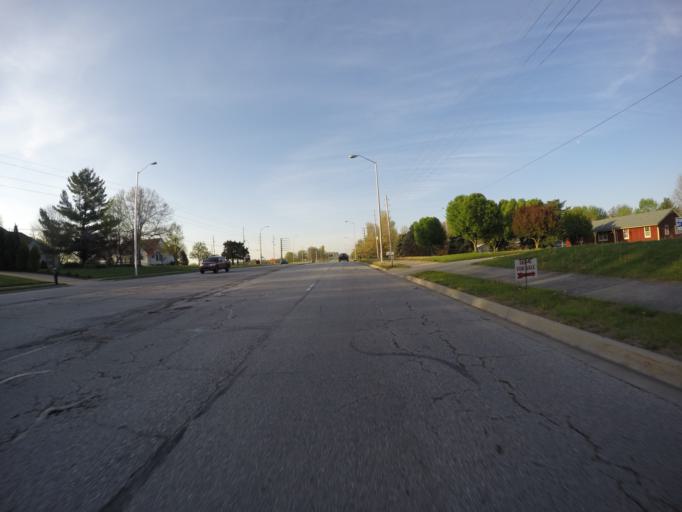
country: US
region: Missouri
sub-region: Jackson County
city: Lees Summit
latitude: 38.9290
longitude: -94.4498
